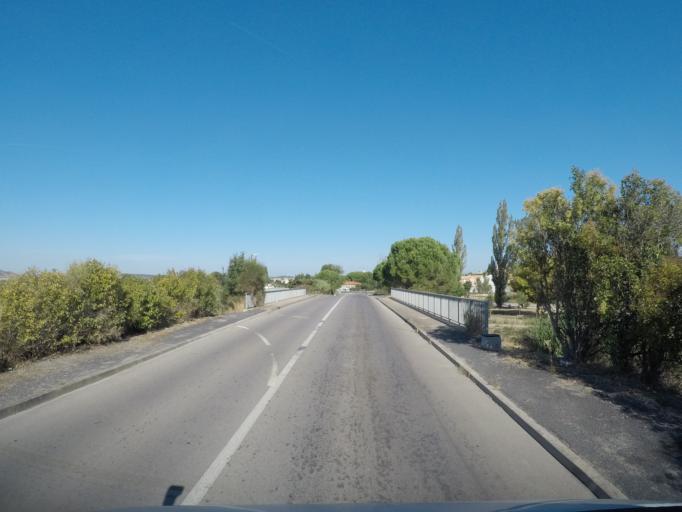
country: FR
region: Languedoc-Roussillon
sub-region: Departement de l'Aude
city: Narbonne
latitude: 43.1721
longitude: 3.0078
